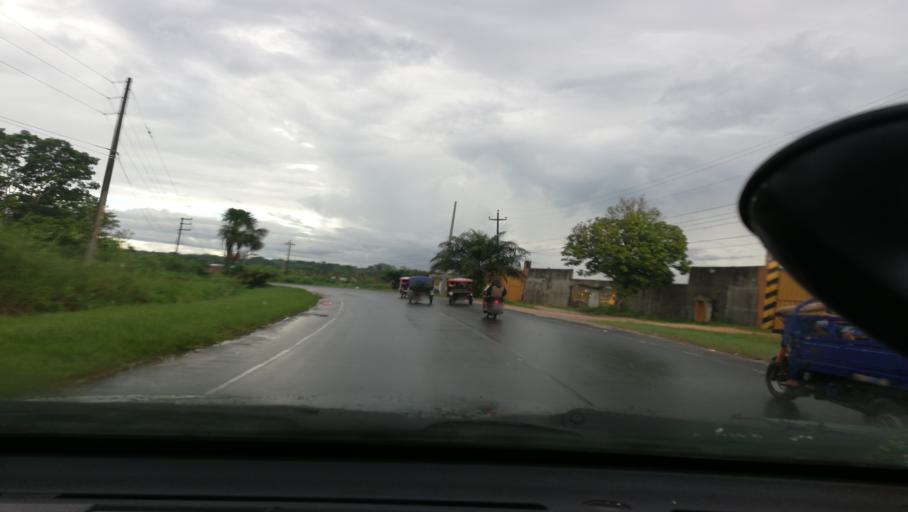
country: PE
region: Loreto
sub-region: Provincia de Maynas
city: Iquitos
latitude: -3.8309
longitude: -73.3280
